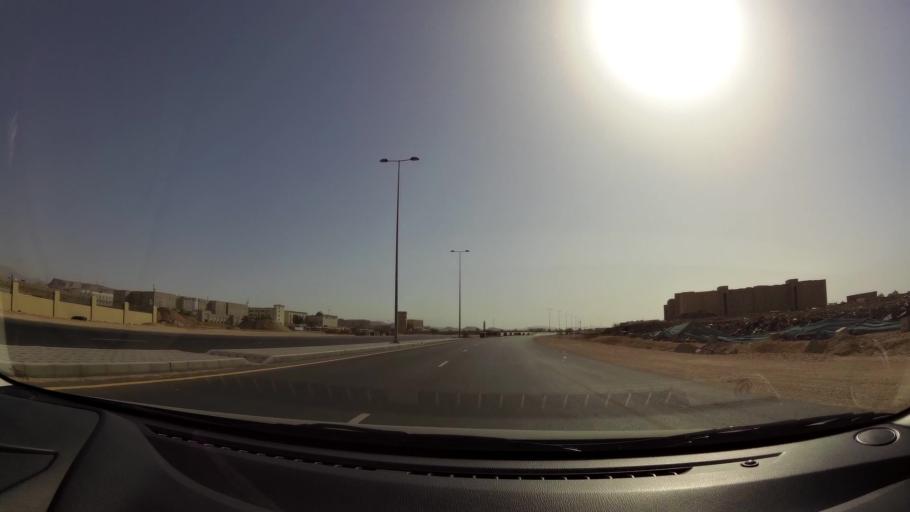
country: OM
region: Muhafazat Masqat
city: Bawshar
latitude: 23.5739
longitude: 58.2866
